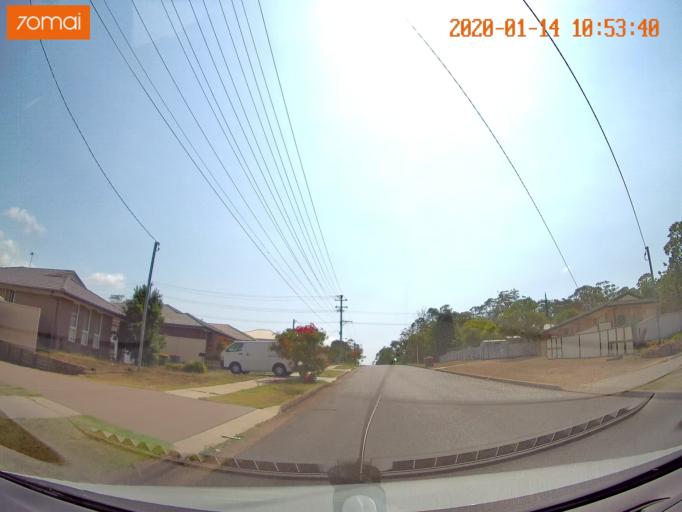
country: AU
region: New South Wales
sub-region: Lake Macquarie Shire
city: Dora Creek
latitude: -33.1012
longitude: 151.4875
